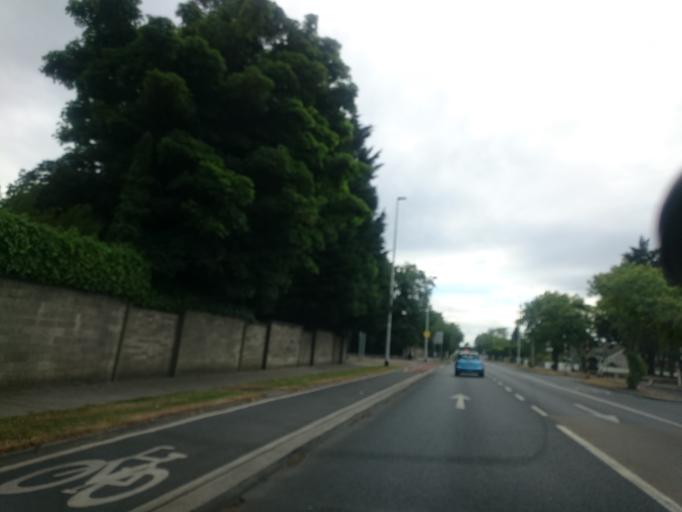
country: IE
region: Leinster
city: Dundrum
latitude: 53.2942
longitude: -6.2513
